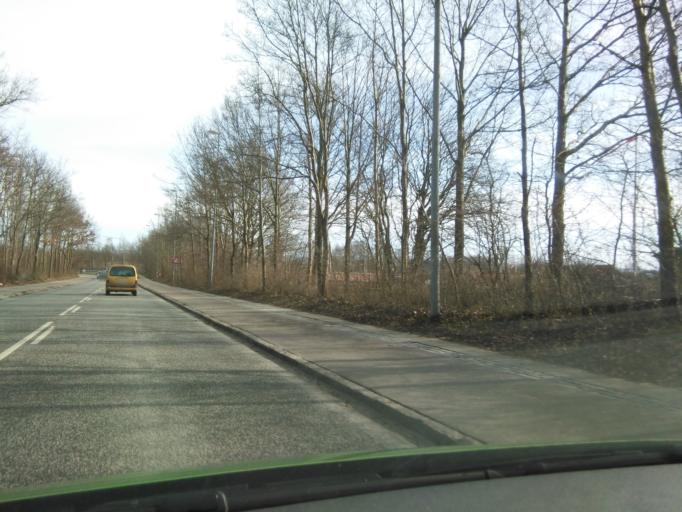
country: DK
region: Central Jutland
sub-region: Arhus Kommune
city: Arhus
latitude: 56.1895
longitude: 10.2014
